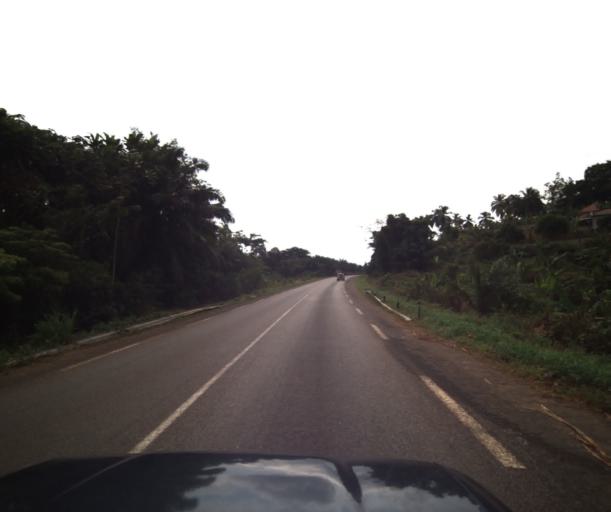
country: CM
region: Littoral
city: Edea
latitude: 3.8387
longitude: 10.4527
